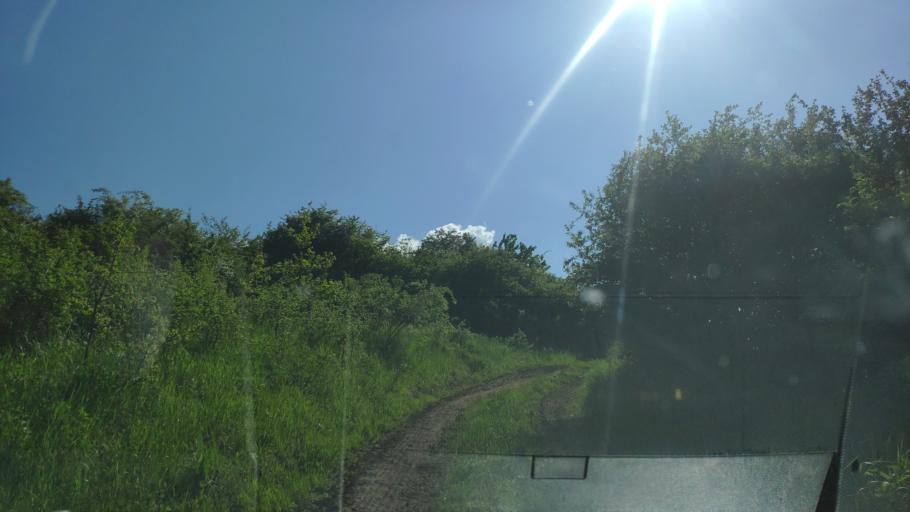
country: SK
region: Presovsky
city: Sabinov
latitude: 49.0524
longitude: 21.1463
